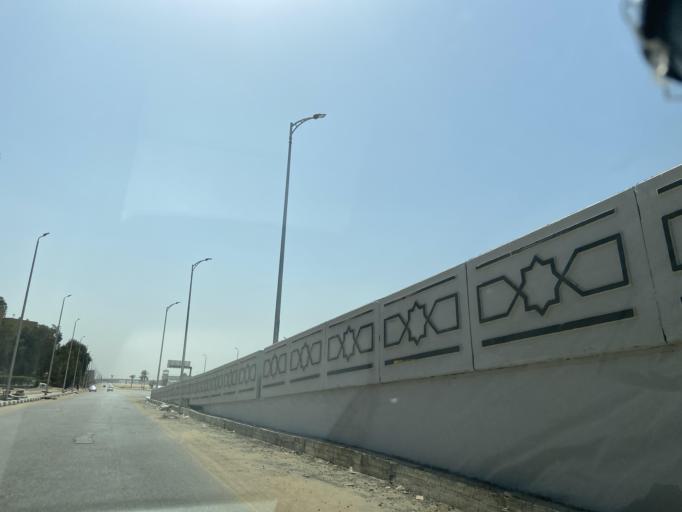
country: EG
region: Muhafazat al Qahirah
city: Cairo
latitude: 30.0459
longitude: 31.3651
